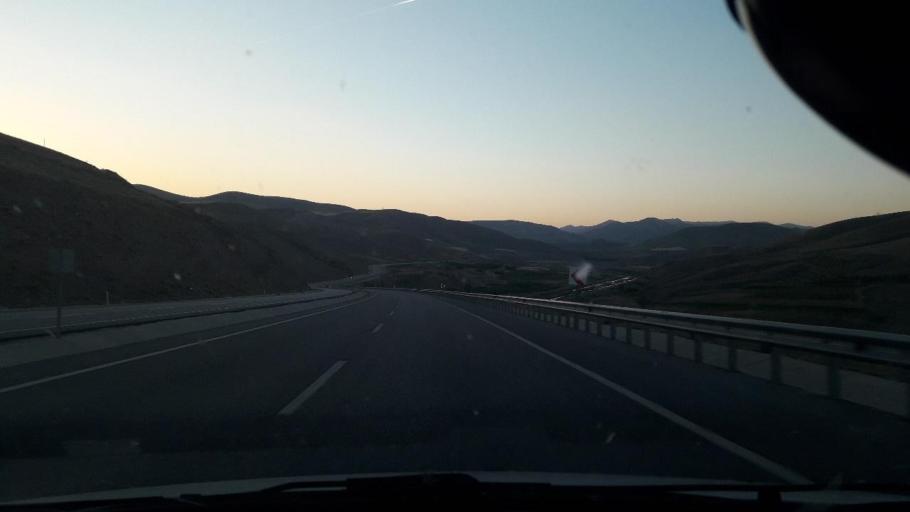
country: TR
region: Malatya
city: Yazihan
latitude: 38.6195
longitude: 38.1702
